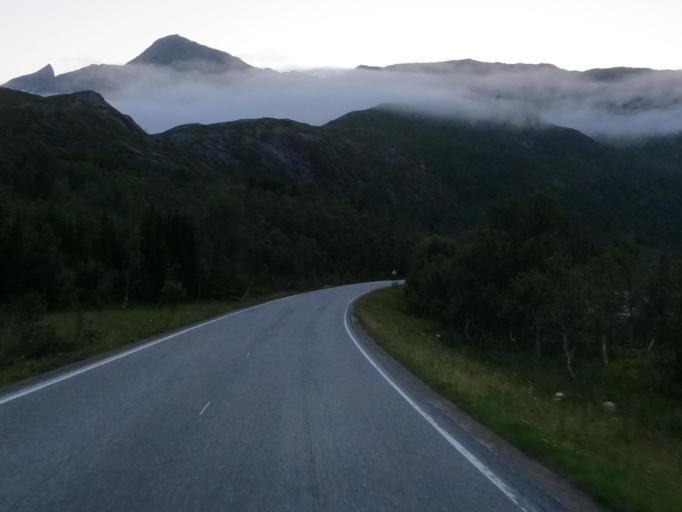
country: NO
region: Nordland
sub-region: Lodingen
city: Lodingen
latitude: 68.5327
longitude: 15.7248
